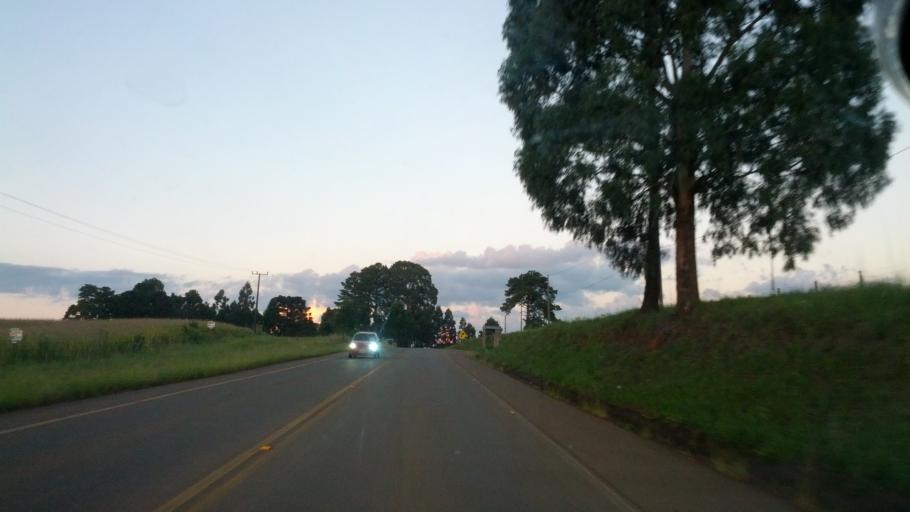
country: BR
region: Rio Grande do Sul
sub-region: Vacaria
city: Estrela
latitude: -27.8978
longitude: -50.7762
